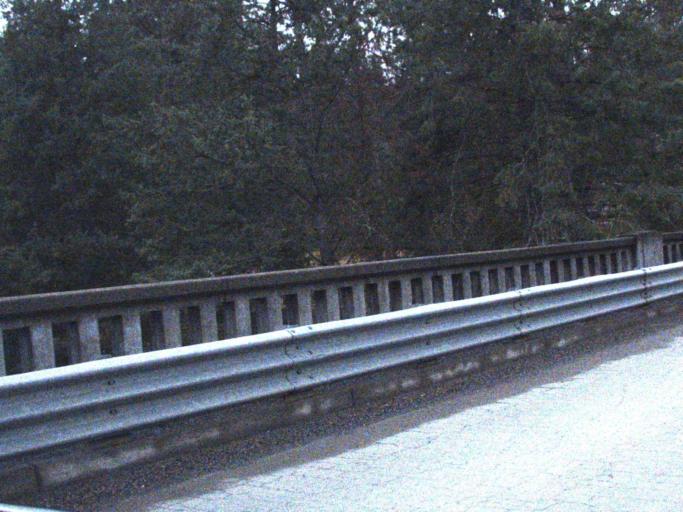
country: US
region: Washington
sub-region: Spokane County
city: Fairchild Air Force Base
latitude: 47.8386
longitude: -117.8525
